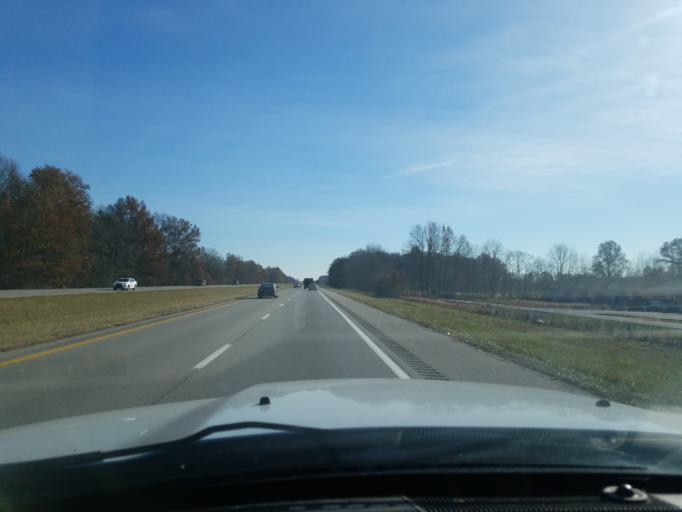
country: US
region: Ohio
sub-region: Brown County
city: Mount Orab
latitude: 39.0547
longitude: -83.9771
